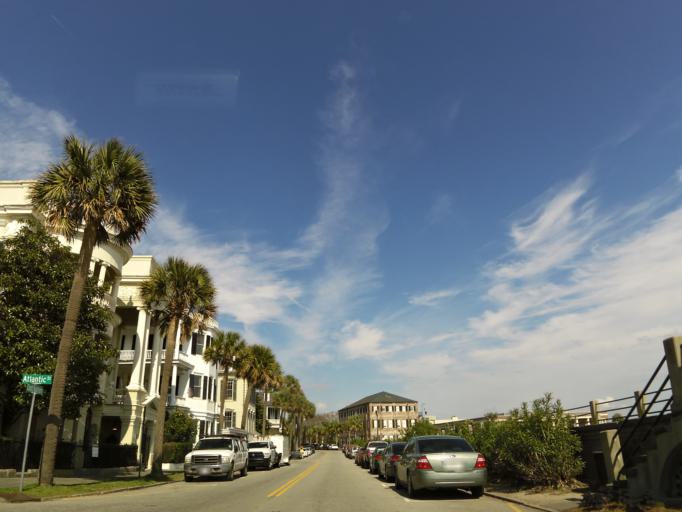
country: US
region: South Carolina
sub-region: Charleston County
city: Charleston
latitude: 32.7720
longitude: -79.9278
